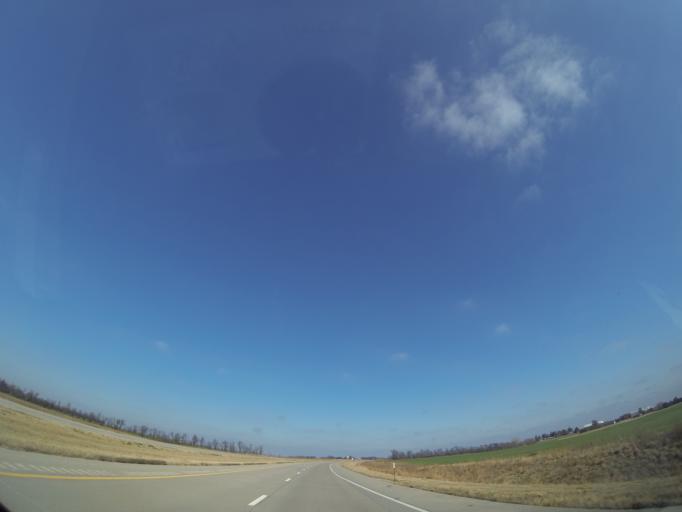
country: US
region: Kansas
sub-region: McPherson County
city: Inman
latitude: 38.2365
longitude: -97.7826
